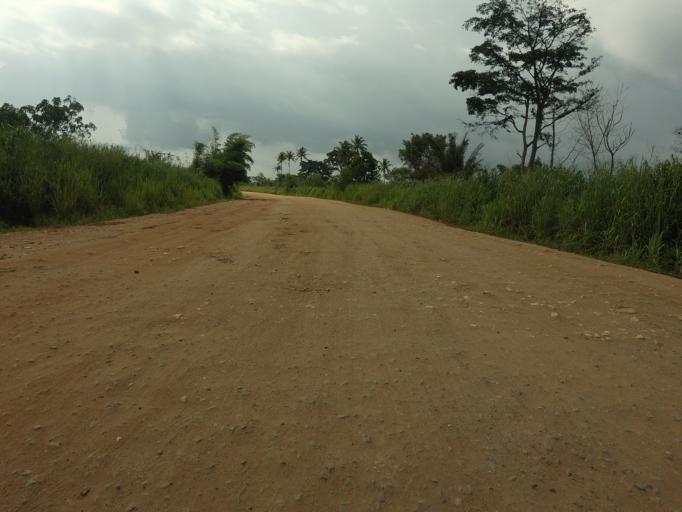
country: GH
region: Volta
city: Kpandu
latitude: 6.9840
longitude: 0.4470
